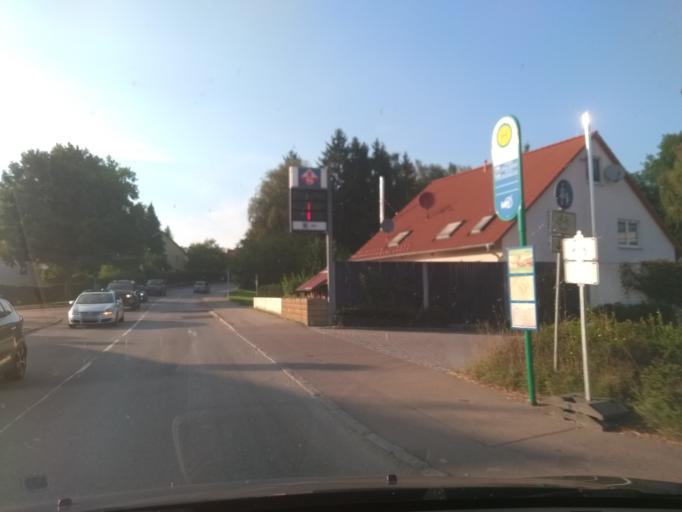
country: DE
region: Bavaria
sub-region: Upper Bavaria
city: Markt Indersdorf
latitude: 48.3260
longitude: 11.3885
